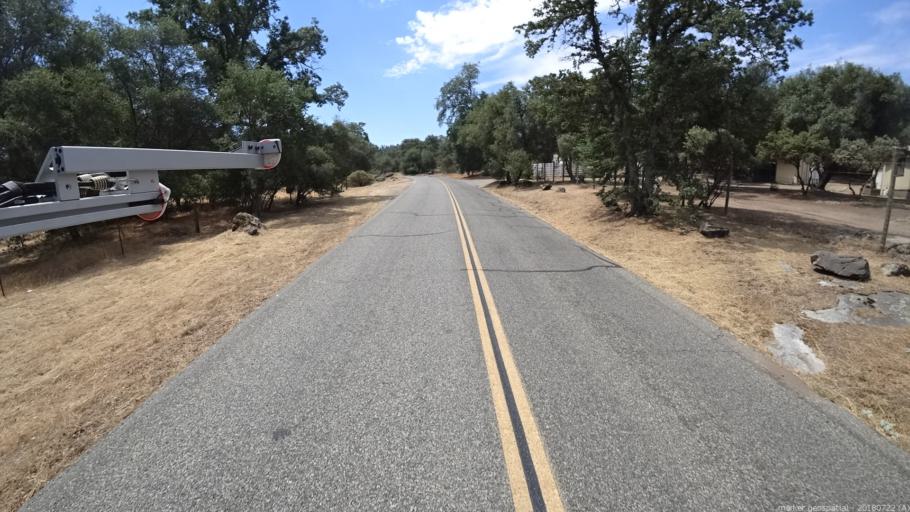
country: US
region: California
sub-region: Madera County
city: Coarsegold
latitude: 37.2578
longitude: -119.7351
